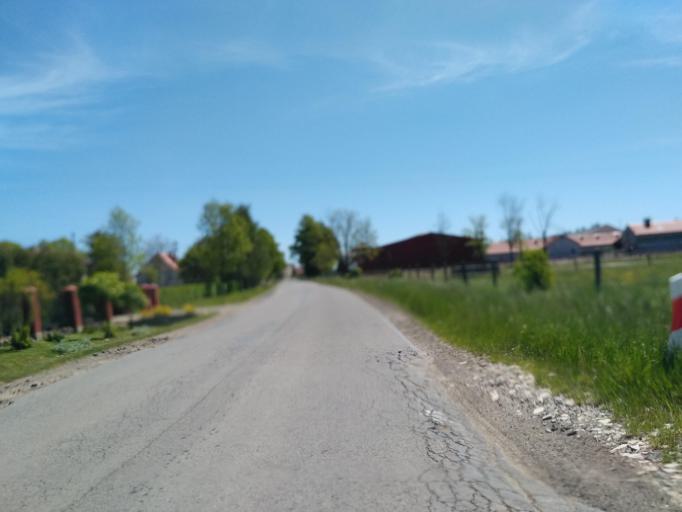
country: PL
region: Subcarpathian Voivodeship
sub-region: Powiat krosnienski
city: Sieniawa
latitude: 49.5414
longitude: 21.9633
